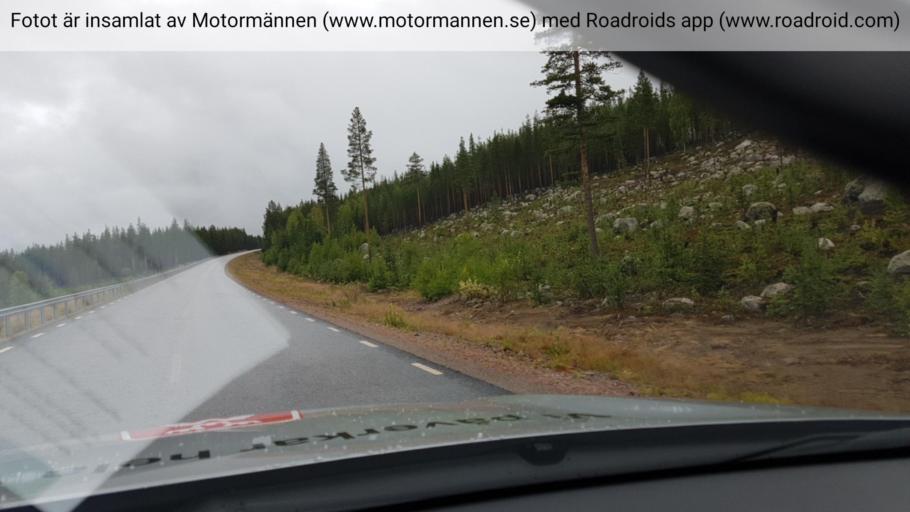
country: SE
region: Norrbotten
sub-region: Gallivare Kommun
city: Gaellivare
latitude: 66.6716
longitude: 20.3687
